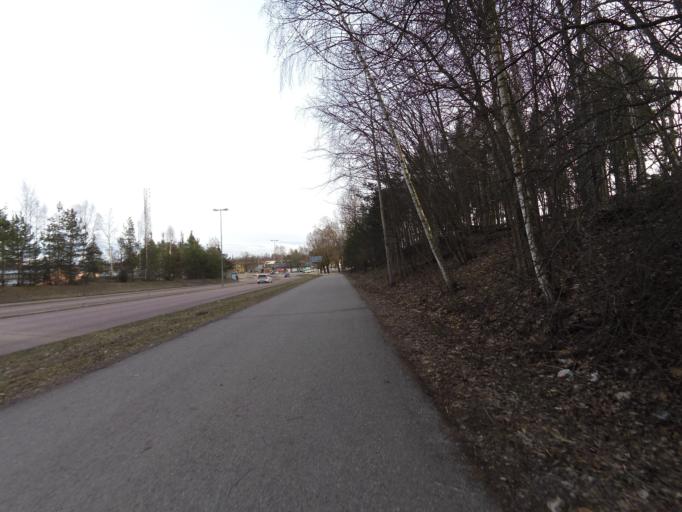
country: SE
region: Gaevleborg
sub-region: Gavle Kommun
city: Gavle
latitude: 60.6805
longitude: 17.1232
